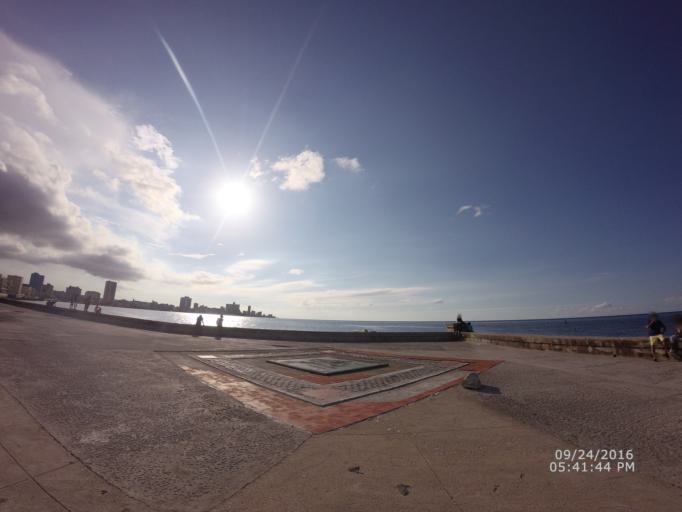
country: CU
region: La Habana
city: Centro Habana
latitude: 23.1468
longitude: -82.3581
